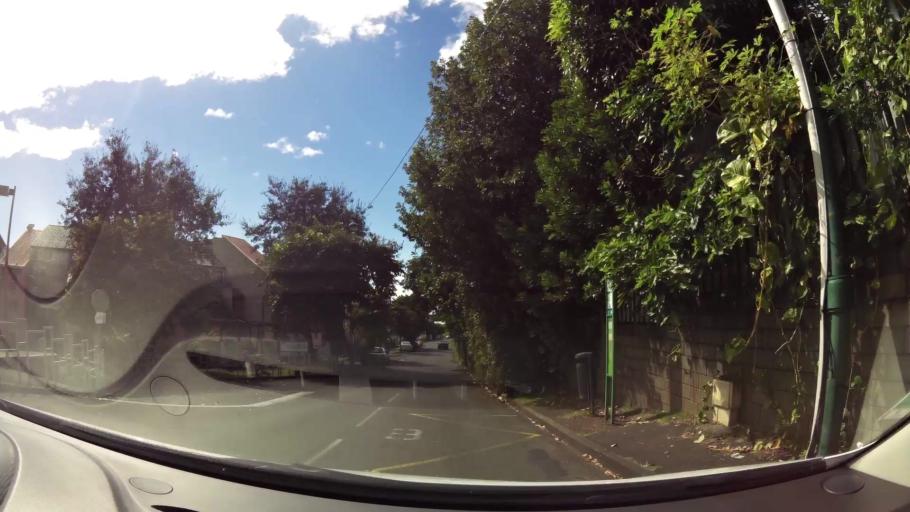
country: RE
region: Reunion
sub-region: Reunion
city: Saint-Denis
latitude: -20.9263
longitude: 55.4889
